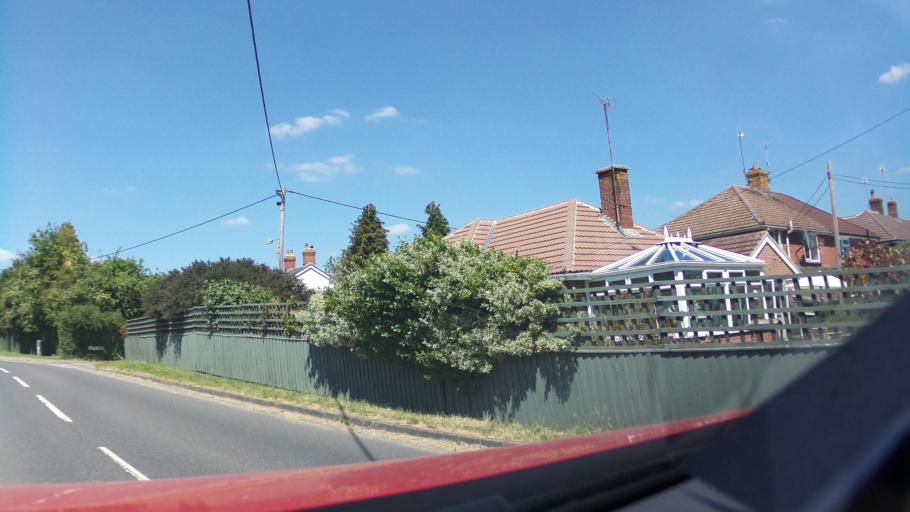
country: GB
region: England
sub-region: Wiltshire
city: Royal Wootton Bassett
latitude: 51.5324
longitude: -1.8999
